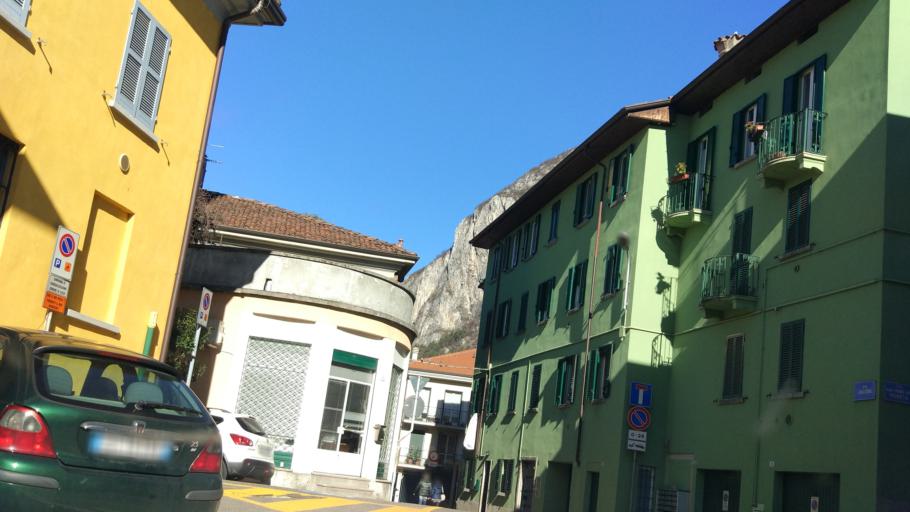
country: IT
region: Lombardy
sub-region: Provincia di Lecco
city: Lecco
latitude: 45.8609
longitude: 9.3967
